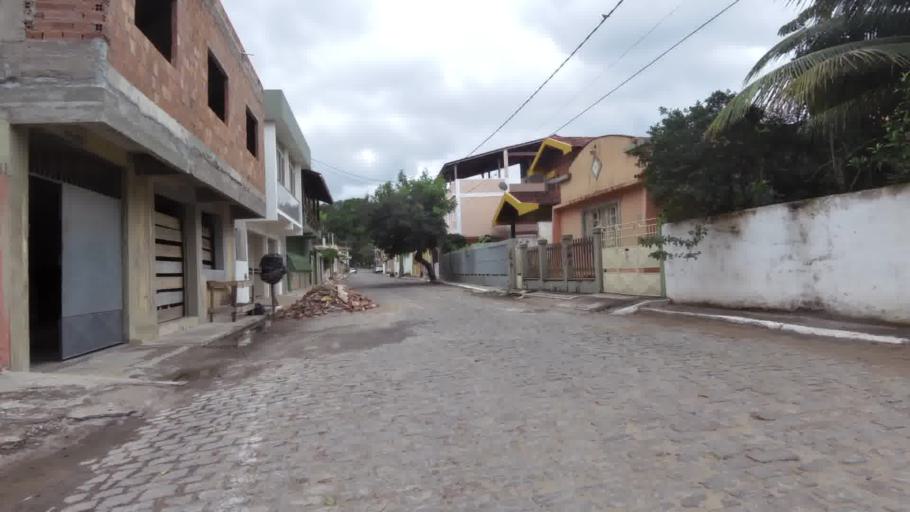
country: BR
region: Espirito Santo
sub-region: Marataizes
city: Marataizes
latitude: -21.0429
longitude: -40.8264
